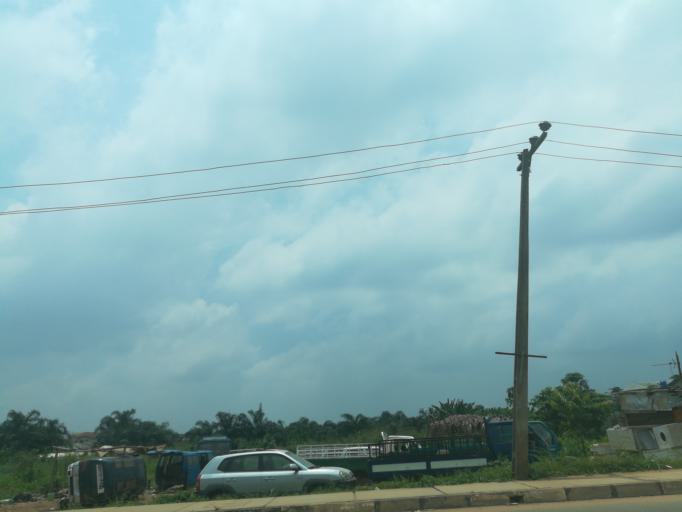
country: NG
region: Lagos
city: Ikorodu
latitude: 6.6244
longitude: 3.5255
